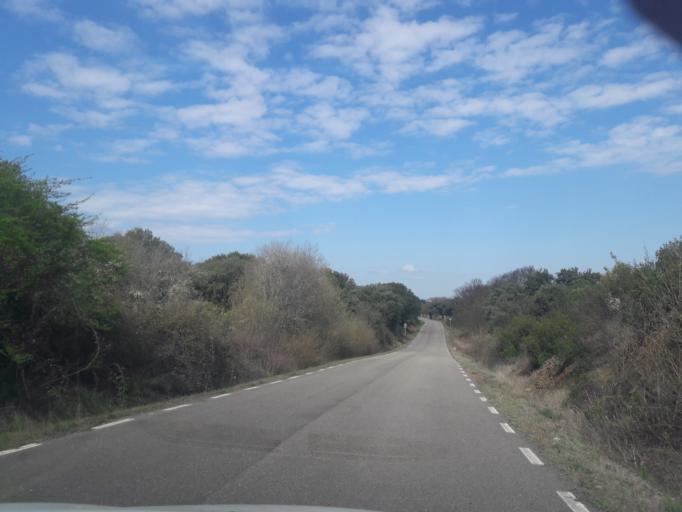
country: ES
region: Castille and Leon
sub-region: Provincia de Salamanca
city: Zamarra
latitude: 40.5519
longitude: -6.4421
